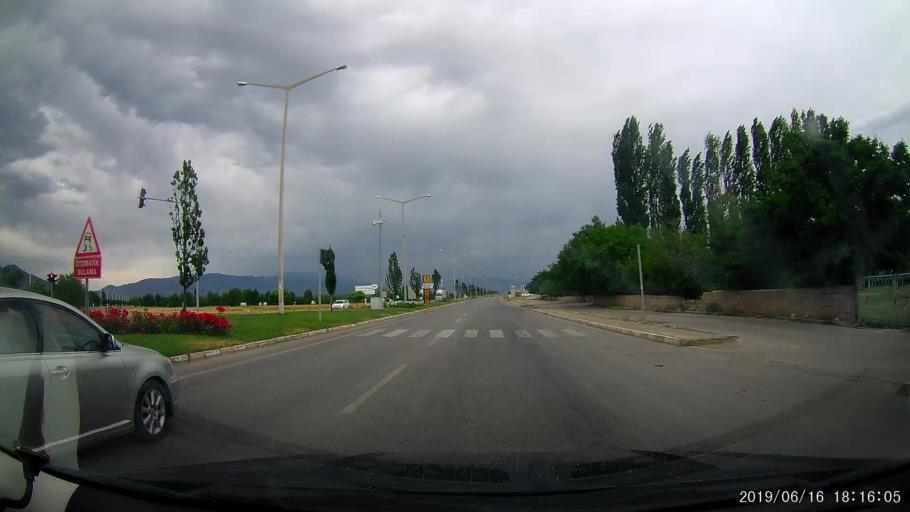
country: TR
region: Erzincan
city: Erzincan
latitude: 39.7268
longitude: 39.5522
